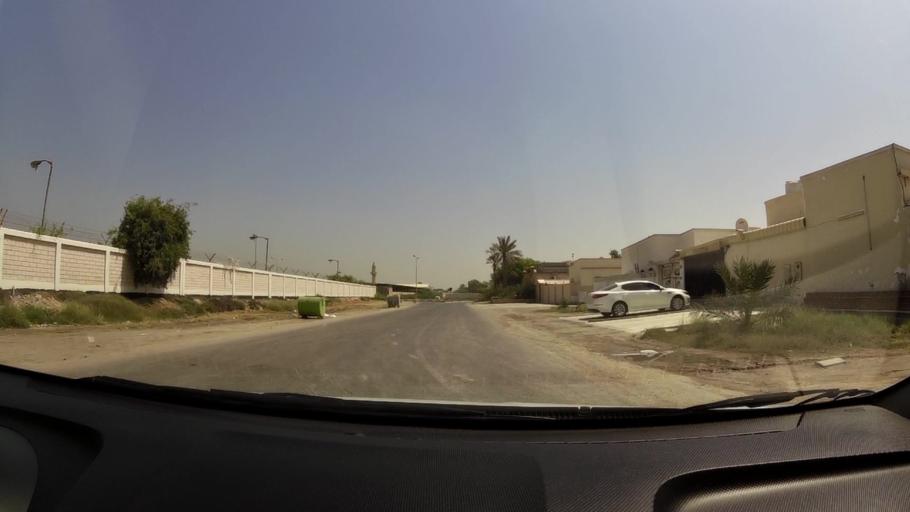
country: AE
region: Umm al Qaywayn
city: Umm al Qaywayn
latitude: 25.5548
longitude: 55.5527
